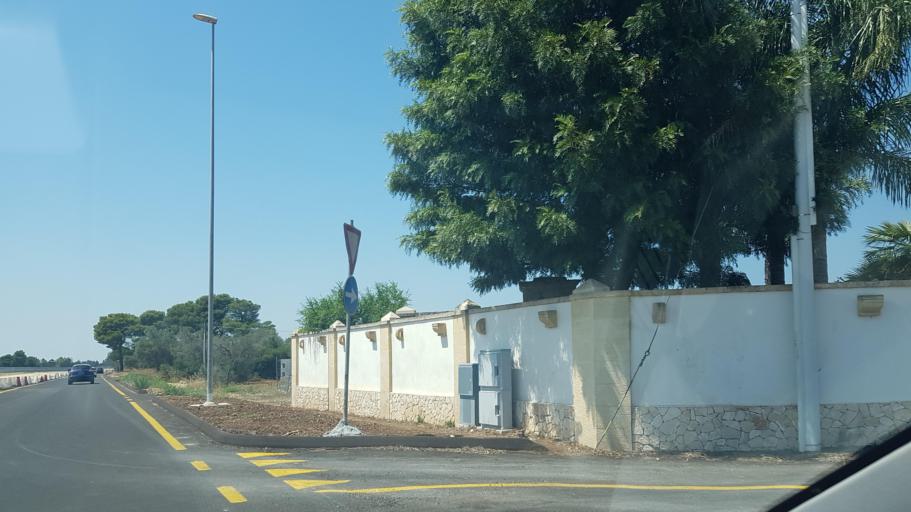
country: IT
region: Apulia
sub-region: Provincia di Lecce
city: Merine
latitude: 40.3280
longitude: 18.2530
